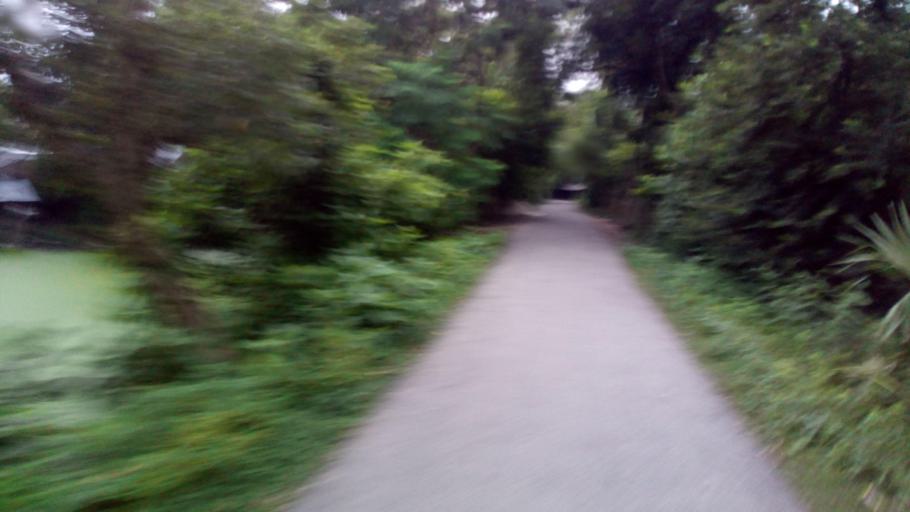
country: BD
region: Khulna
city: Phultala
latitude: 22.7576
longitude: 89.4082
